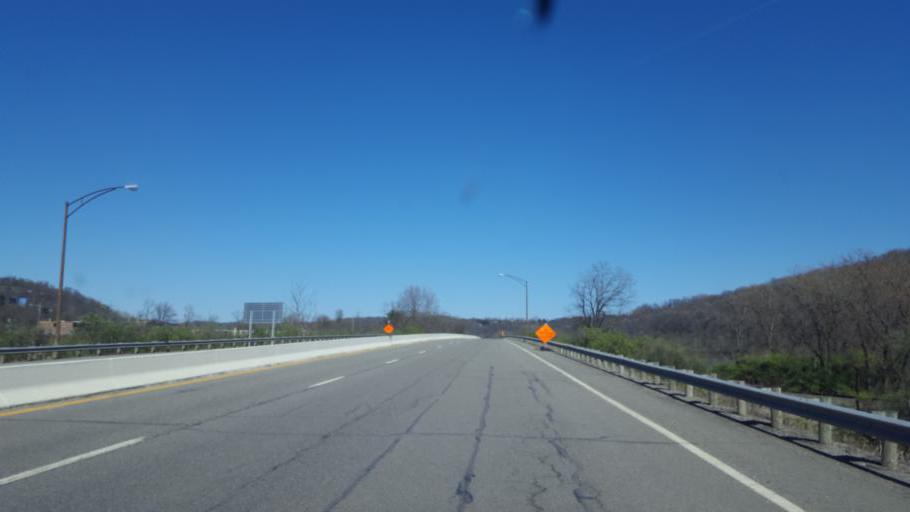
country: US
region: Ohio
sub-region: Jefferson County
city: Brilliant
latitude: 40.2587
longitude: -80.6366
